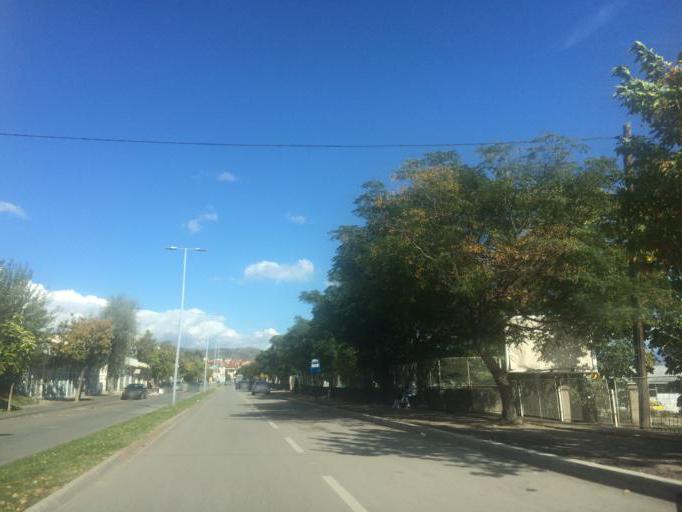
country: MK
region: Kocani
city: Kochani
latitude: 41.9125
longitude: 22.4197
